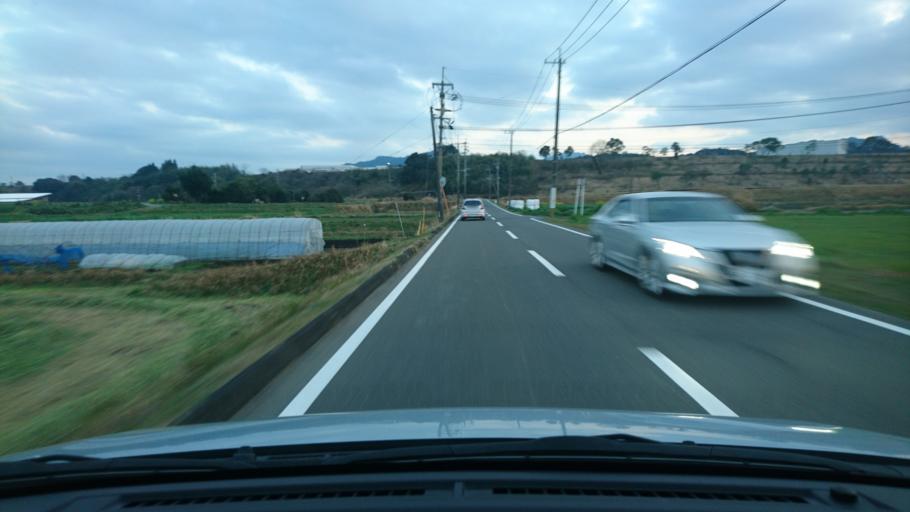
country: JP
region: Miyazaki
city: Miyazaki-shi
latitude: 31.8422
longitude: 131.4071
